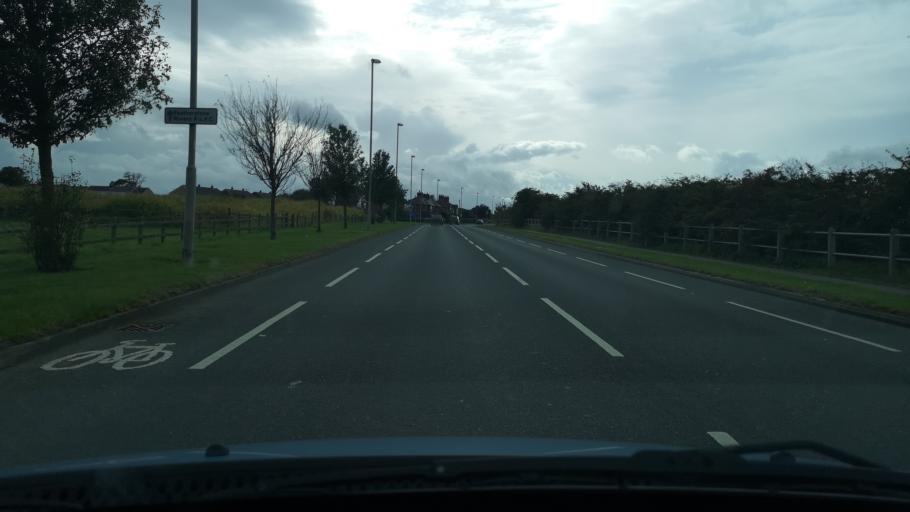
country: GB
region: England
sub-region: City and Borough of Wakefield
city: Featherstone
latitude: 53.6790
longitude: -1.3375
